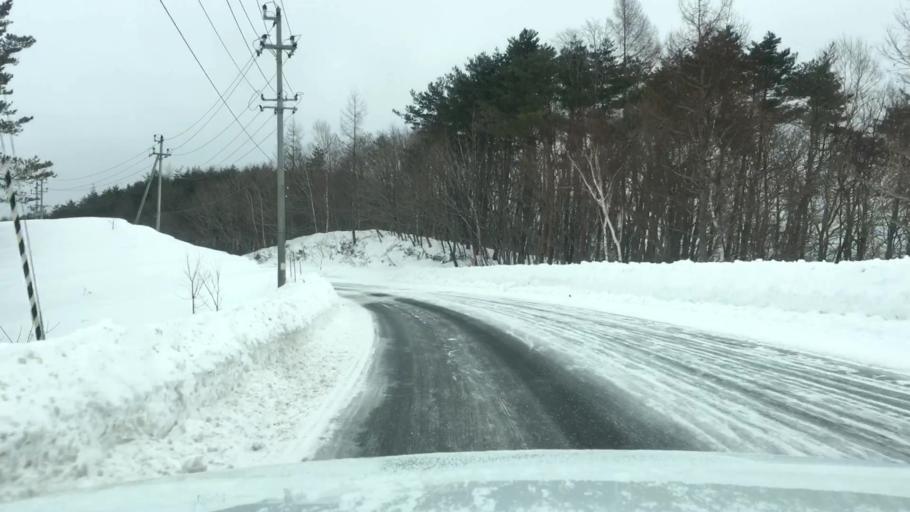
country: JP
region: Iwate
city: Shizukuishi
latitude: 39.9725
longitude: 141.0027
